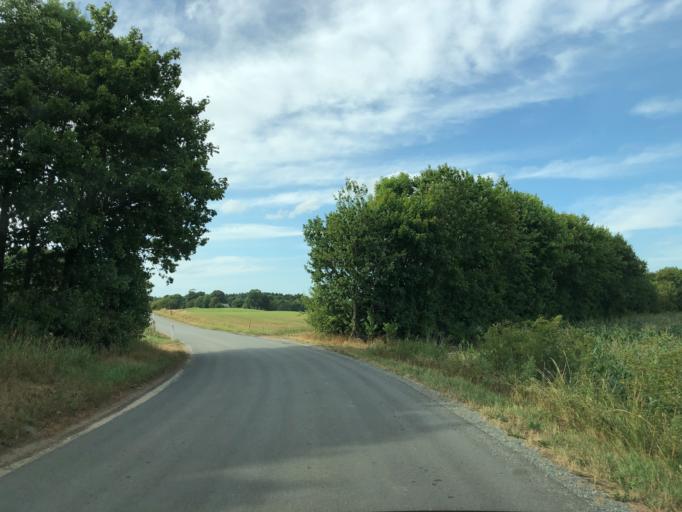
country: DK
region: South Denmark
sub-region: Vejle Kommune
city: Egtved
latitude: 55.6747
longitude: 9.2712
